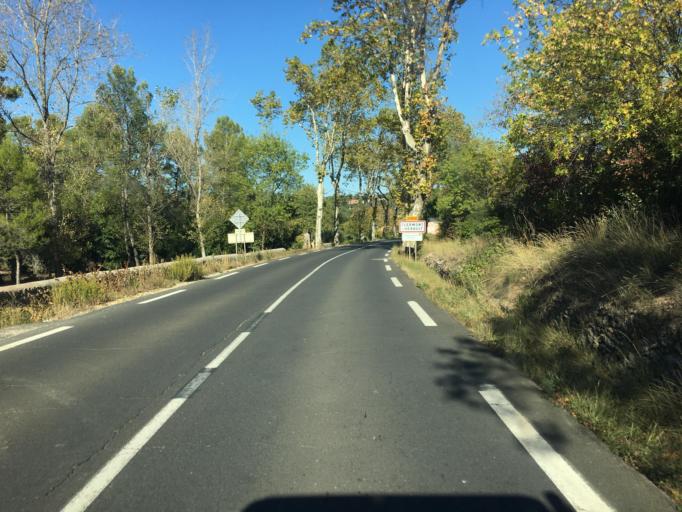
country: FR
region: Languedoc-Roussillon
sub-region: Departement de l'Herault
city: Nebian
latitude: 43.6207
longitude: 3.4120
